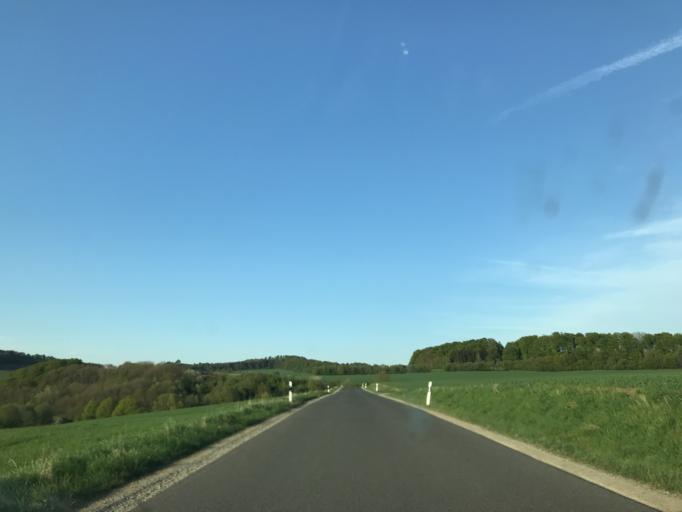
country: DE
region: Thuringia
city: Heuthen
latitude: 51.3359
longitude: 10.2318
